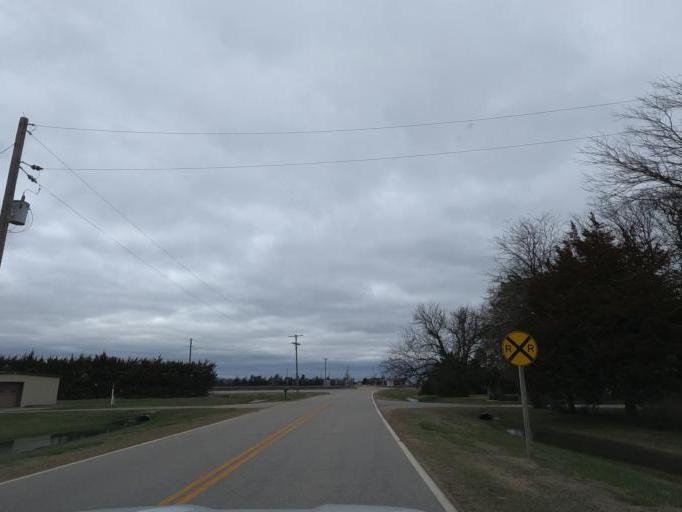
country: US
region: Kansas
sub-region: Reno County
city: South Hutchinson
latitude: 37.9864
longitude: -98.0502
